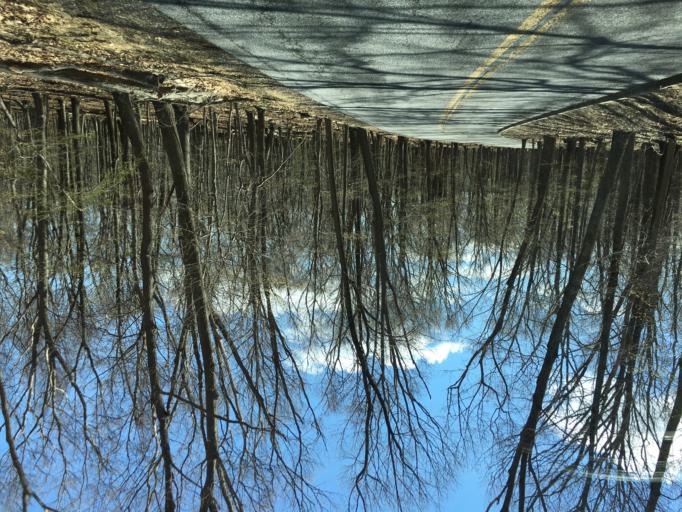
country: US
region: Maryland
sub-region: Washington County
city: Highfield-Cascade
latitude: 39.6475
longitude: -77.4761
